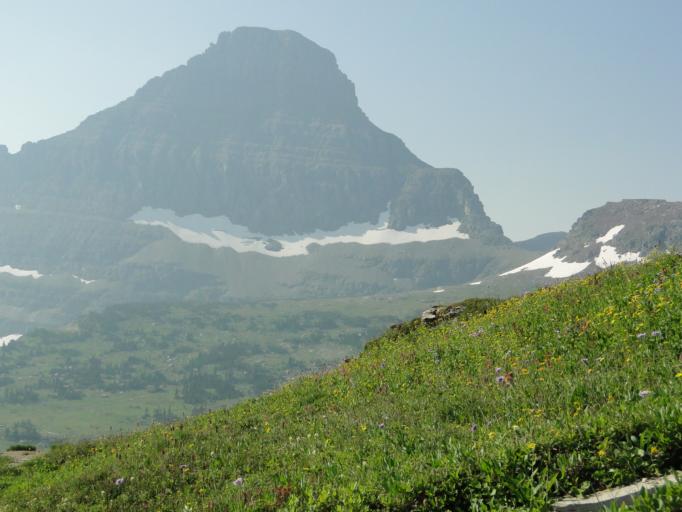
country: US
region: Montana
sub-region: Flathead County
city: Columbia Falls
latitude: 48.6930
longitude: -113.7281
